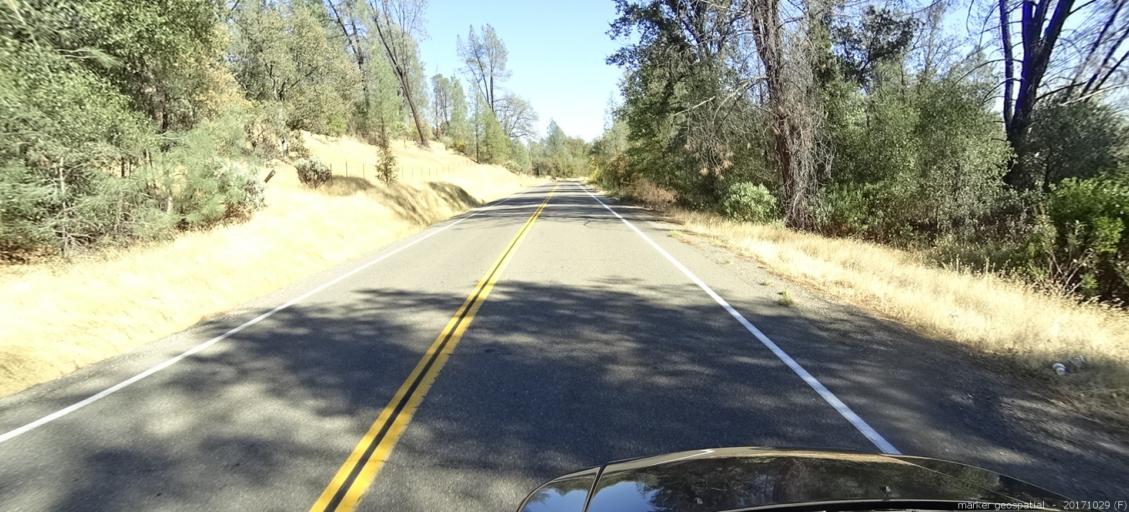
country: US
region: California
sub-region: Shasta County
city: Shasta
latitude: 40.5002
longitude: -122.4572
